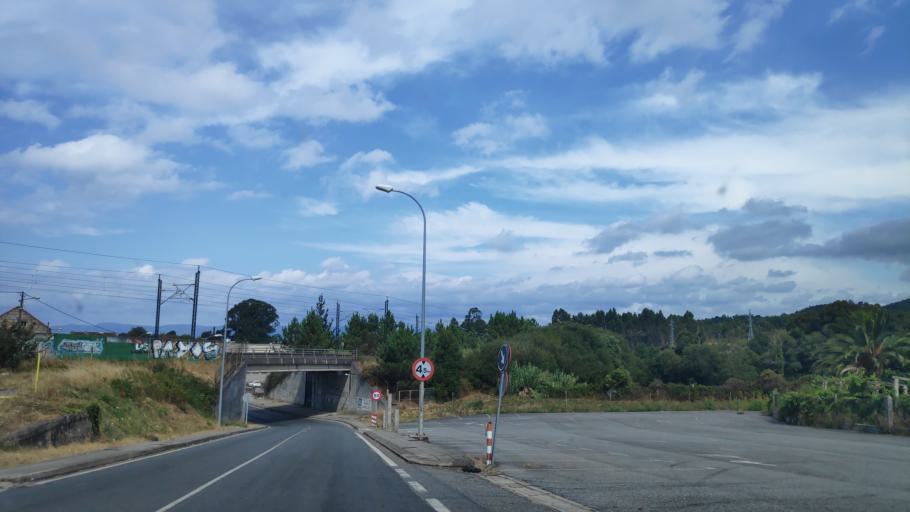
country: ES
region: Galicia
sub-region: Provincia de Pontevedra
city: Vilagarcia de Arousa
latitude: 42.5928
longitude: -8.7420
